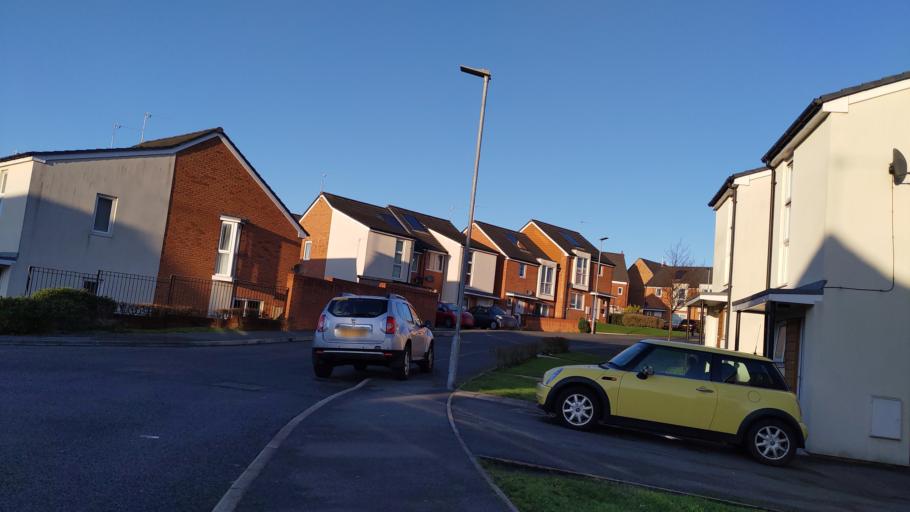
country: GB
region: England
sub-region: Lancashire
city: Adlington
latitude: 53.6196
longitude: -2.6058
